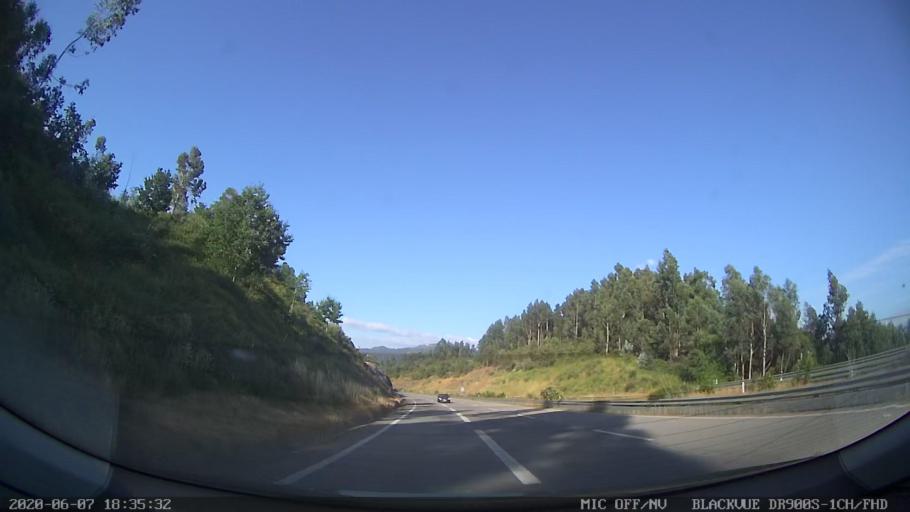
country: PT
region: Braga
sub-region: Guimaraes
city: Serzedo
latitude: 41.3970
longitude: -8.2380
